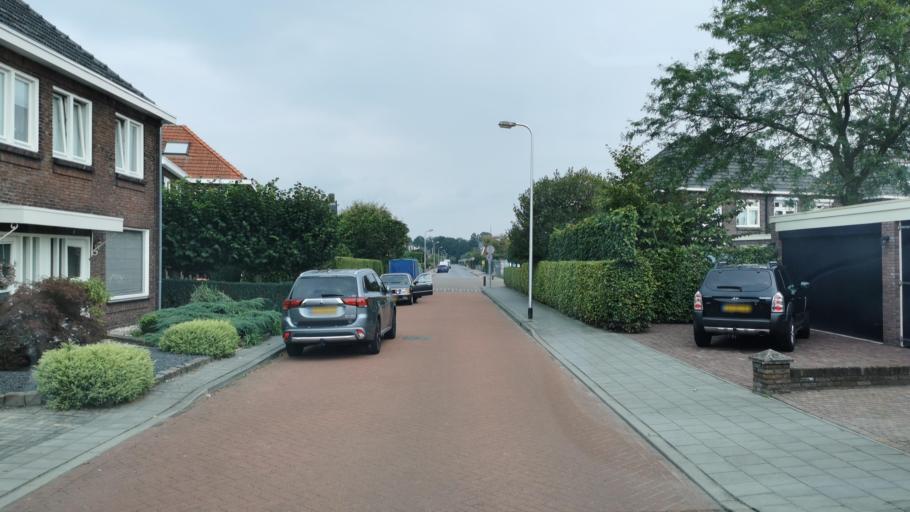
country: NL
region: Overijssel
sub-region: Gemeente Losser
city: Losser
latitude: 52.2676
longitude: 7.0064
